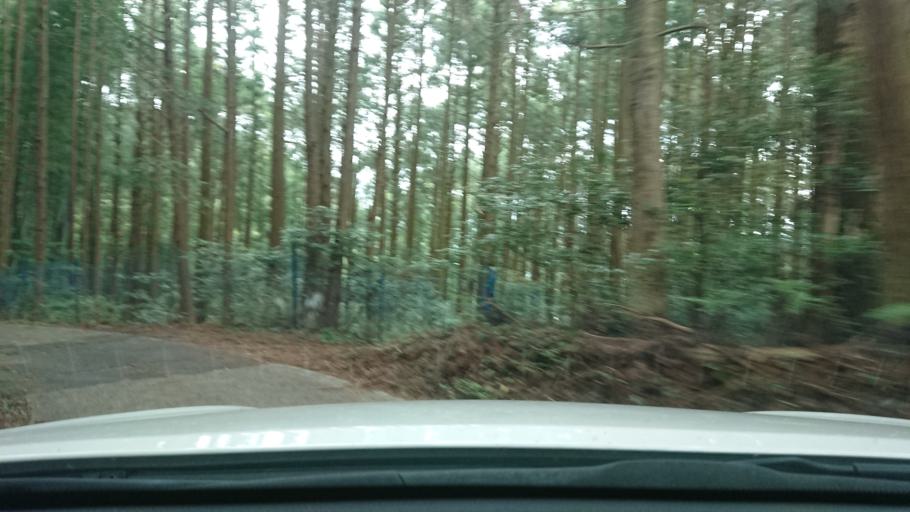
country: JP
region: Tokushima
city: Kamojimacho-jogejima
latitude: 33.8854
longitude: 134.3869
